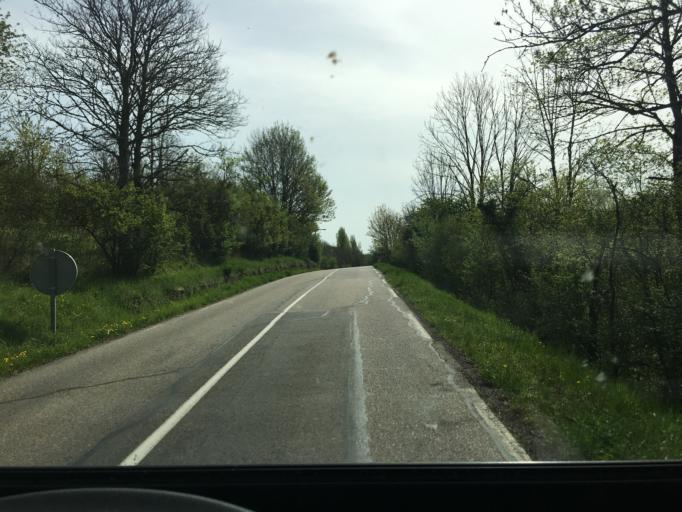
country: FR
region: Lorraine
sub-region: Departement de Meurthe-et-Moselle
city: Chaligny
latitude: 48.6260
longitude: 6.0637
